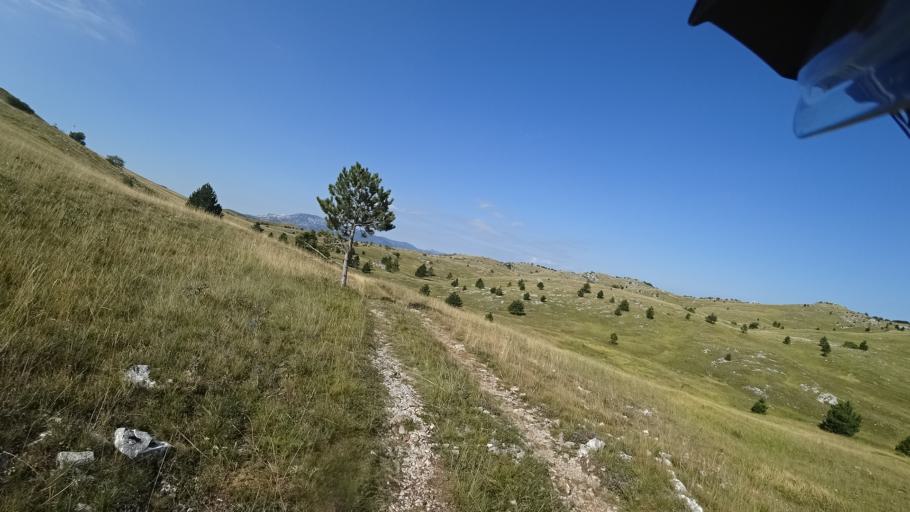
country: HR
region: Zadarska
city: Gracac
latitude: 44.3130
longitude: 15.9894
